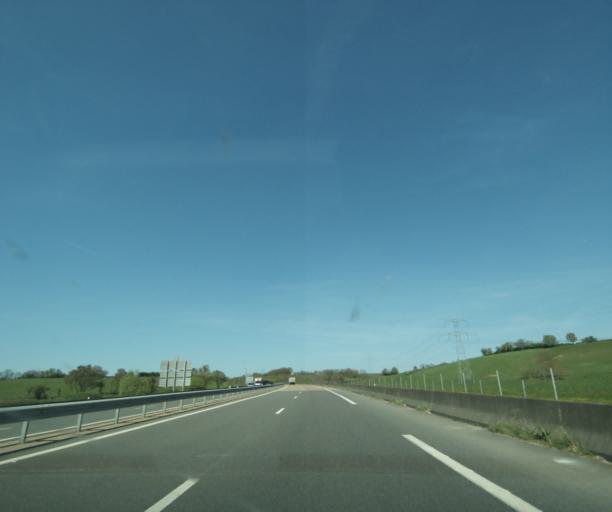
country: FR
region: Bourgogne
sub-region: Departement de la Nievre
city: Pougues-les-Eaux
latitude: 47.0791
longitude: 3.1242
